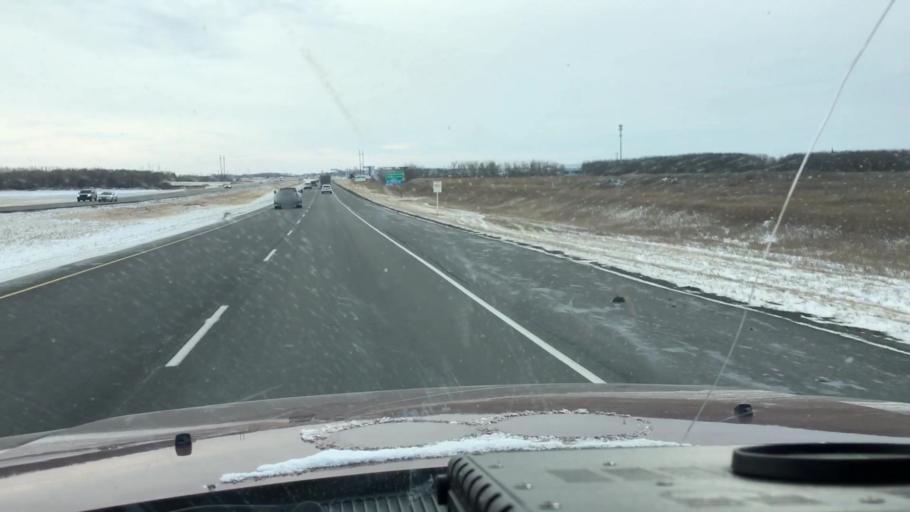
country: CA
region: Saskatchewan
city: Saskatoon
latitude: 52.0668
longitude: -106.6026
